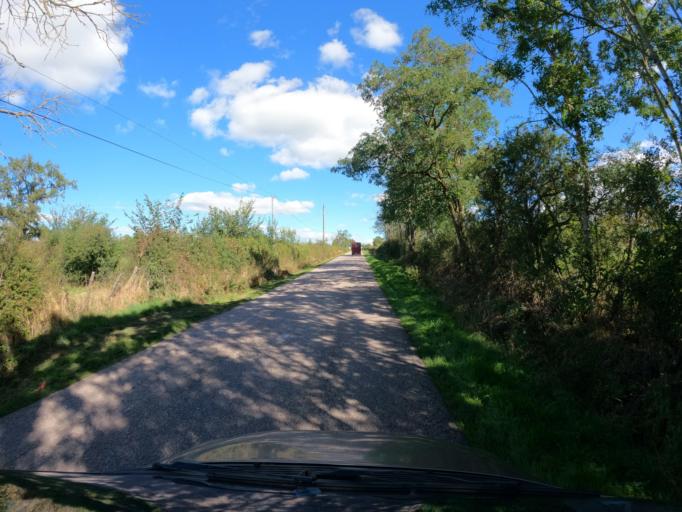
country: FR
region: Auvergne
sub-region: Departement de l'Allier
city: Buxieres-les-Mines
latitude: 46.4043
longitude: 3.0064
